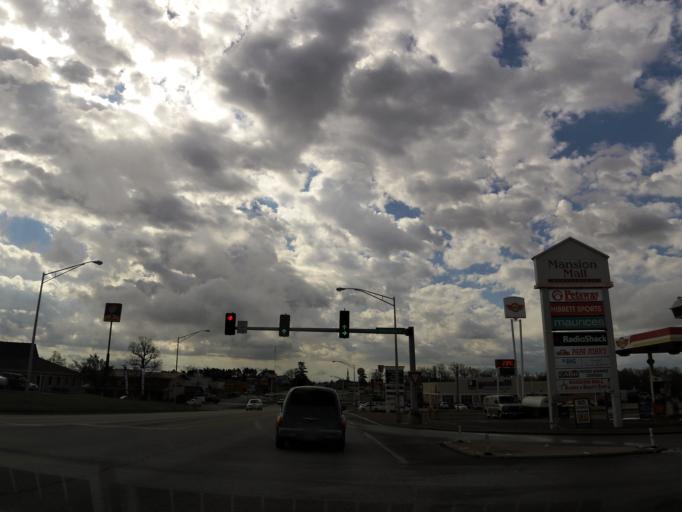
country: US
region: Missouri
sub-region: Butler County
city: Poplar Bluff
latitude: 36.7701
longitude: -90.4171
